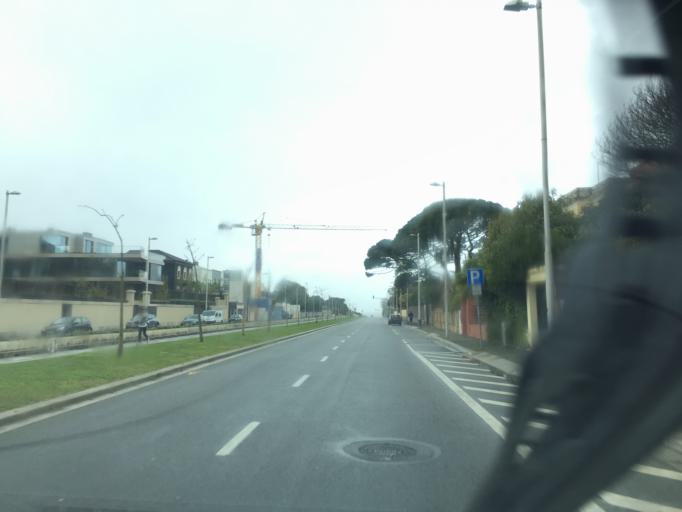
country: PT
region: Porto
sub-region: Matosinhos
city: Matosinhos
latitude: 41.1666
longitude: -8.6797
